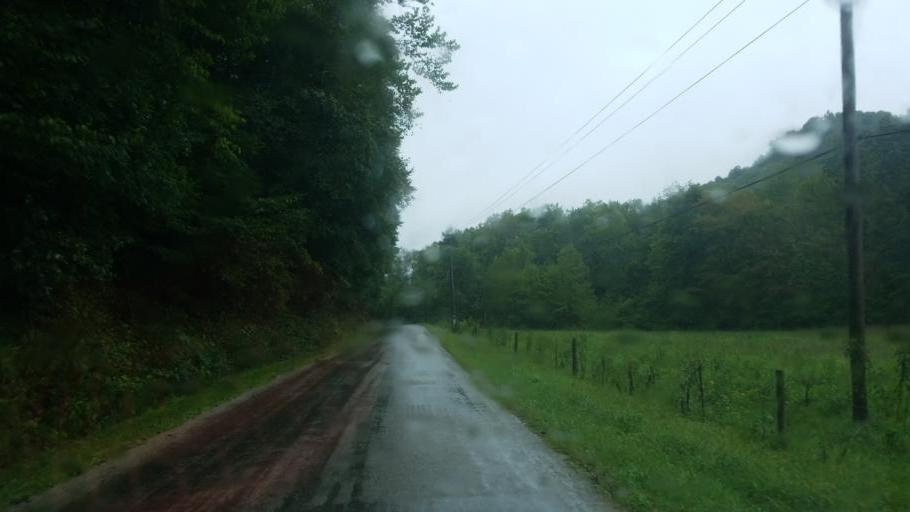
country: US
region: Ohio
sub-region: Adams County
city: Peebles
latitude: 38.8254
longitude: -83.2371
